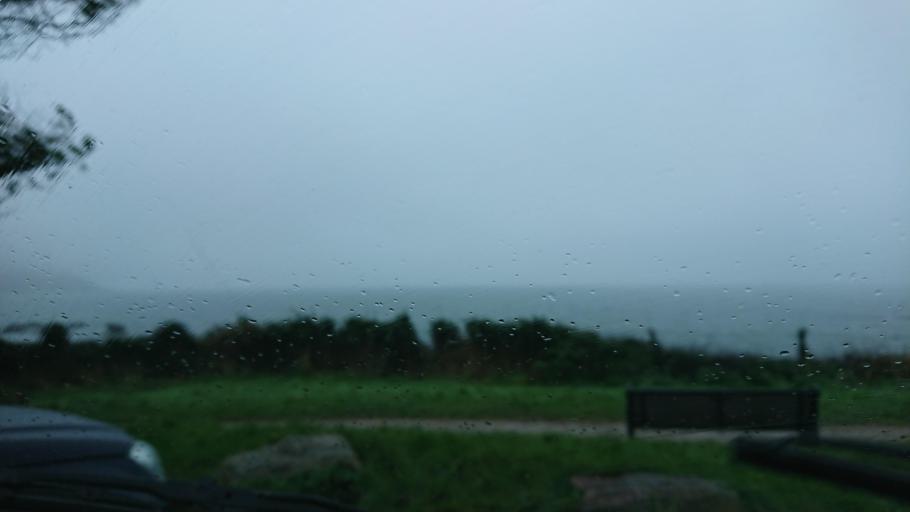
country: GB
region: England
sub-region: Plymouth
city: Plymouth
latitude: 50.3585
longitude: -4.1278
